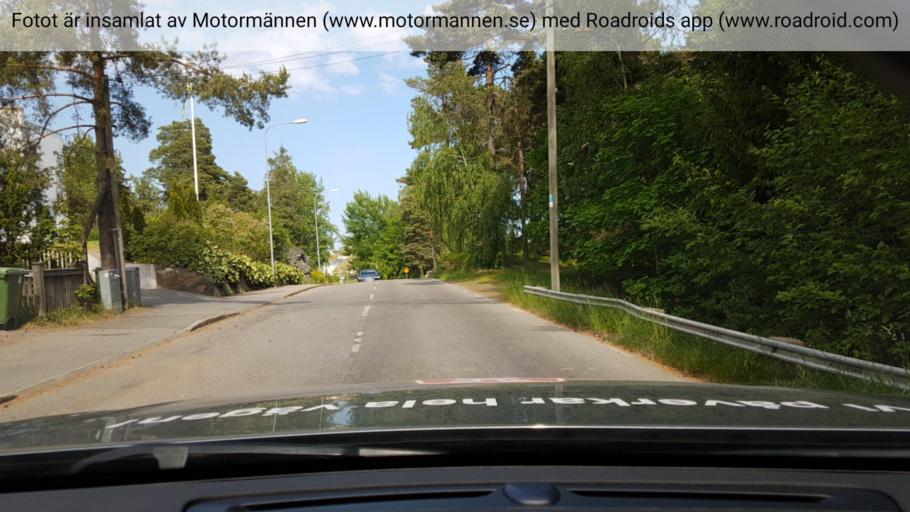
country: SE
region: Stockholm
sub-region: Lidingo
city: Brevik
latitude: 59.3542
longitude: 18.2289
